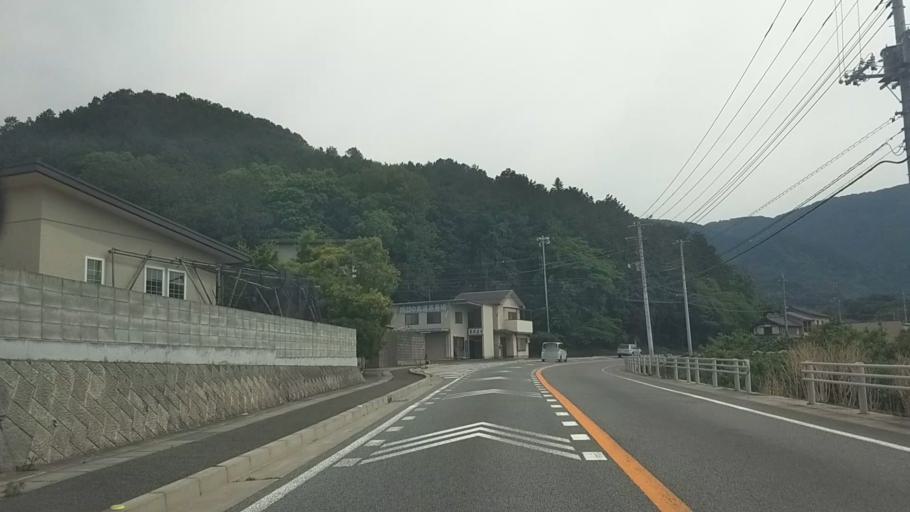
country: JP
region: Yamanashi
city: Isawa
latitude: 35.5789
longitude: 138.5932
